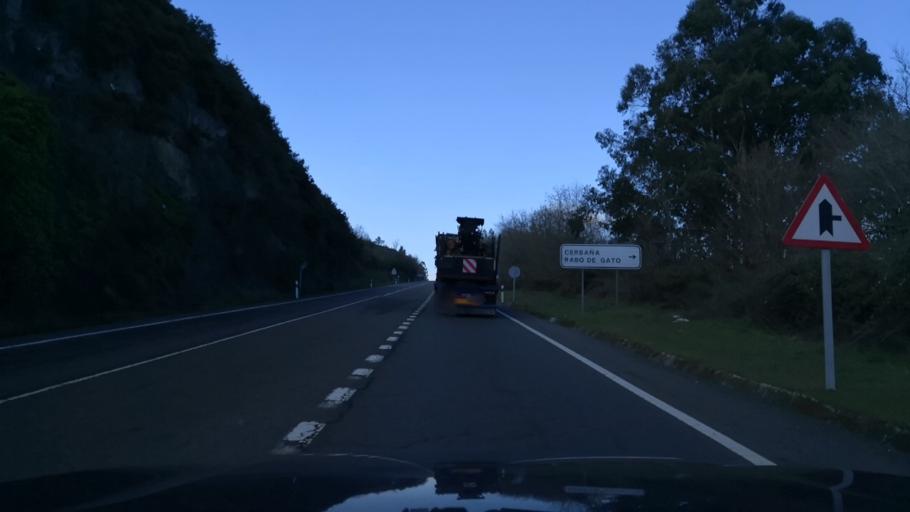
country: ES
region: Galicia
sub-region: Provincia de Pontevedra
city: Silleda
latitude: 42.7007
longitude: -8.3396
